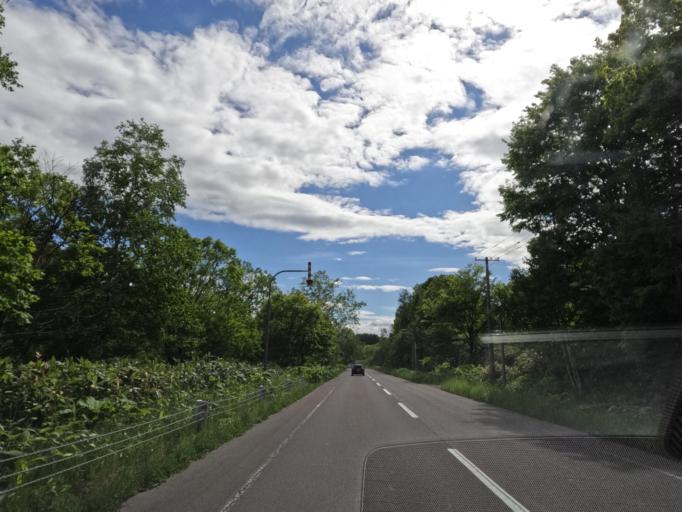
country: JP
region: Hokkaido
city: Kamikawa
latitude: 43.8783
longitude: 142.5747
